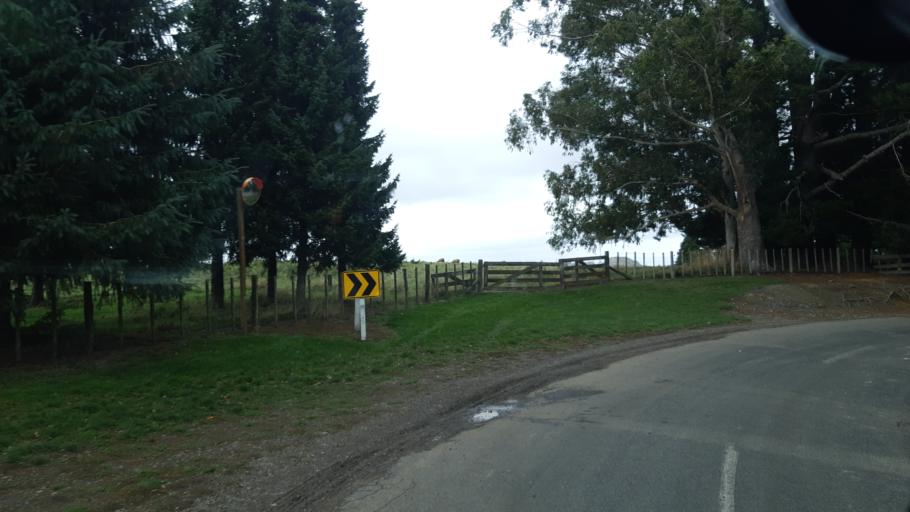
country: NZ
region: Manawatu-Wanganui
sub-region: Ruapehu District
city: Waiouru
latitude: -39.6147
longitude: 175.6470
